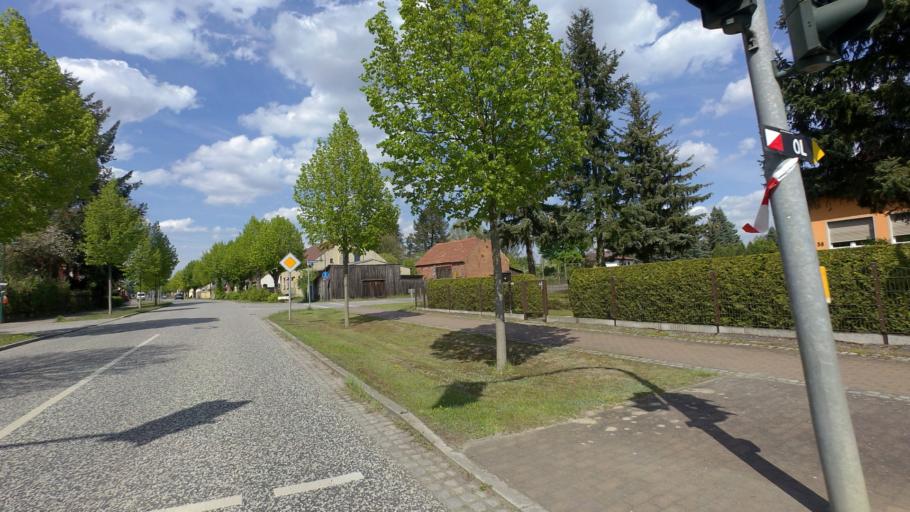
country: DE
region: Brandenburg
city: Marienwerder
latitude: 52.9012
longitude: 13.5359
